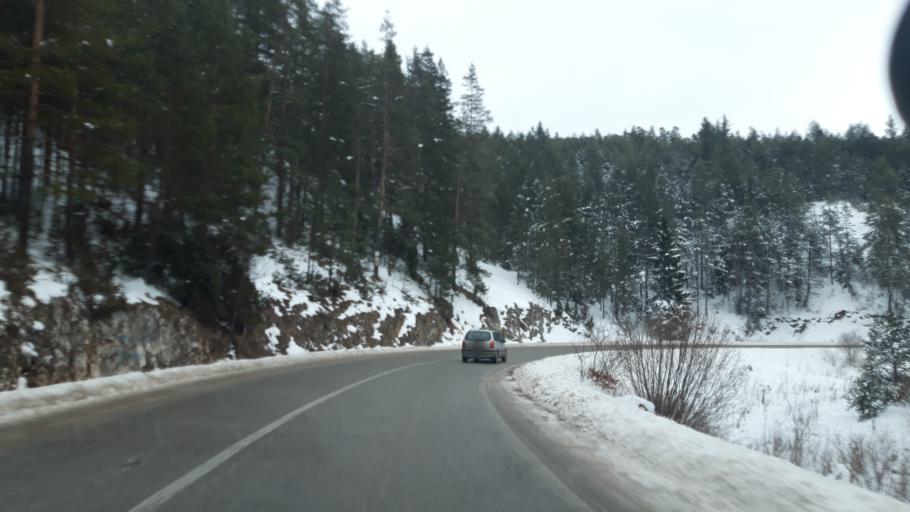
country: BA
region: Republika Srpska
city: Sokolac
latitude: 43.9852
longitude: 18.8639
